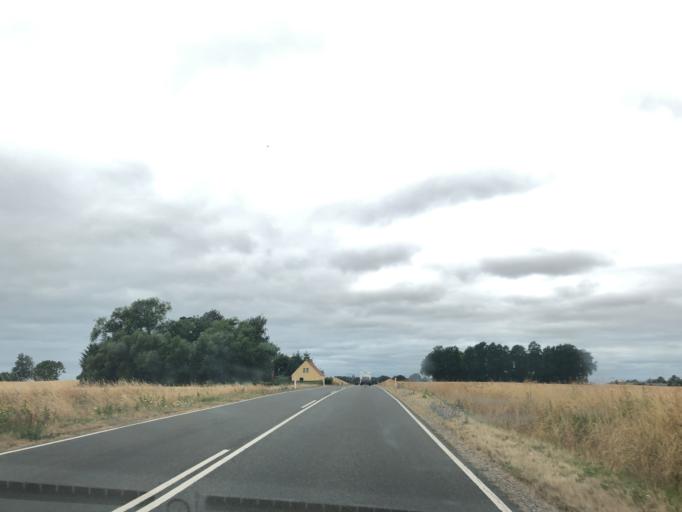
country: DK
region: Zealand
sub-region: Slagelse Kommune
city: Skaelskor
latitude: 55.3011
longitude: 11.3077
